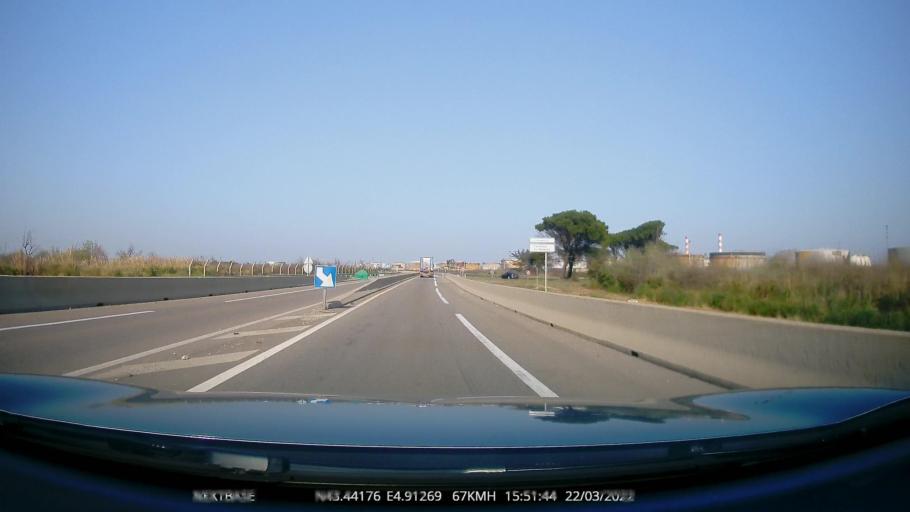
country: FR
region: Provence-Alpes-Cote d'Azur
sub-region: Departement des Bouches-du-Rhone
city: Fos-sur-Mer
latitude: 43.4420
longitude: 4.9131
